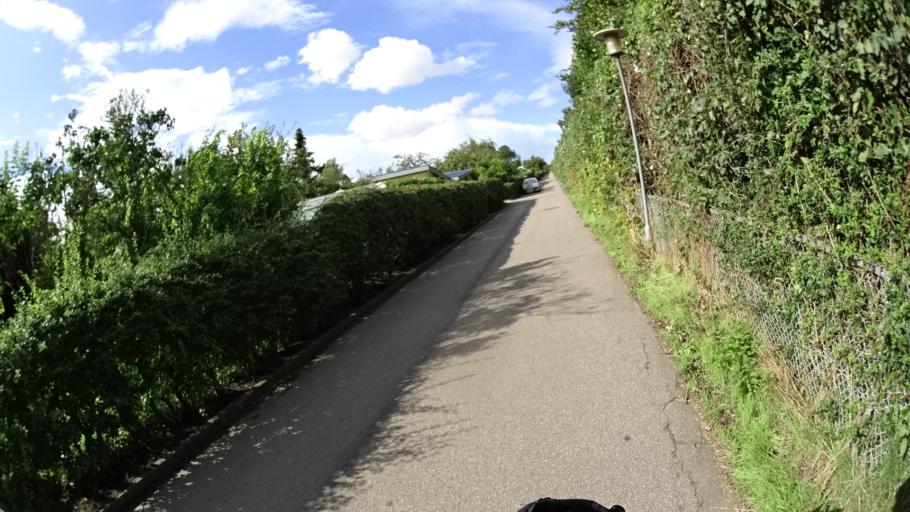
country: DK
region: Central Jutland
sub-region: Arhus Kommune
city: Arhus
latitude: 56.1585
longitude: 10.1785
